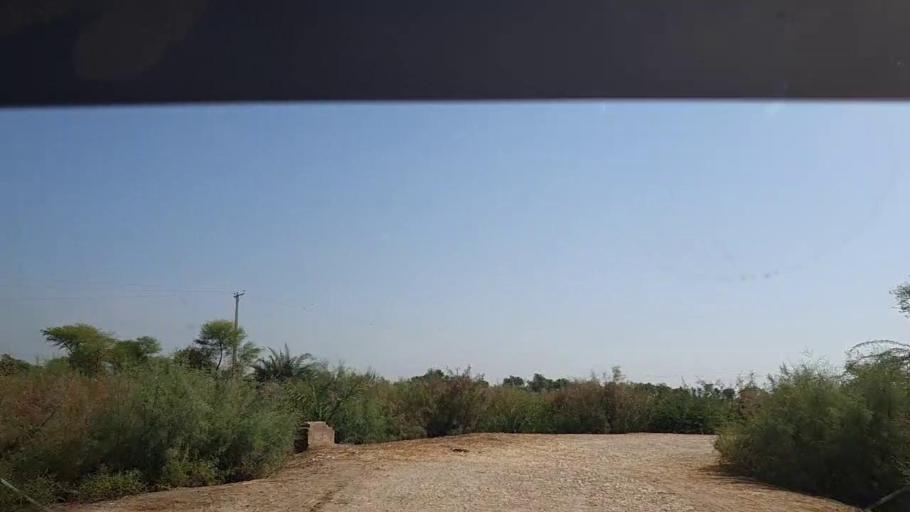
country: PK
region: Sindh
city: Ghauspur
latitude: 28.2172
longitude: 69.0927
